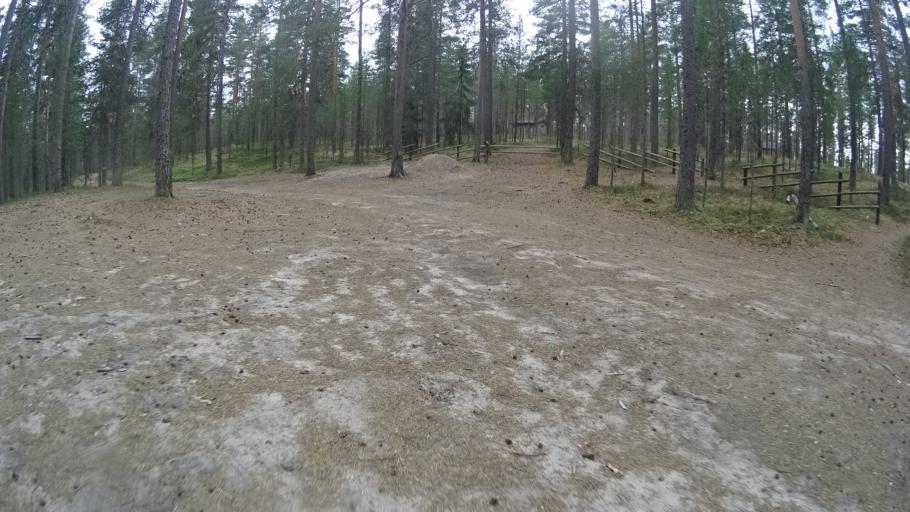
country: FI
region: Satakunta
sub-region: Pohjois-Satakunta
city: Jaemijaervi
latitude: 61.7703
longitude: 22.7872
